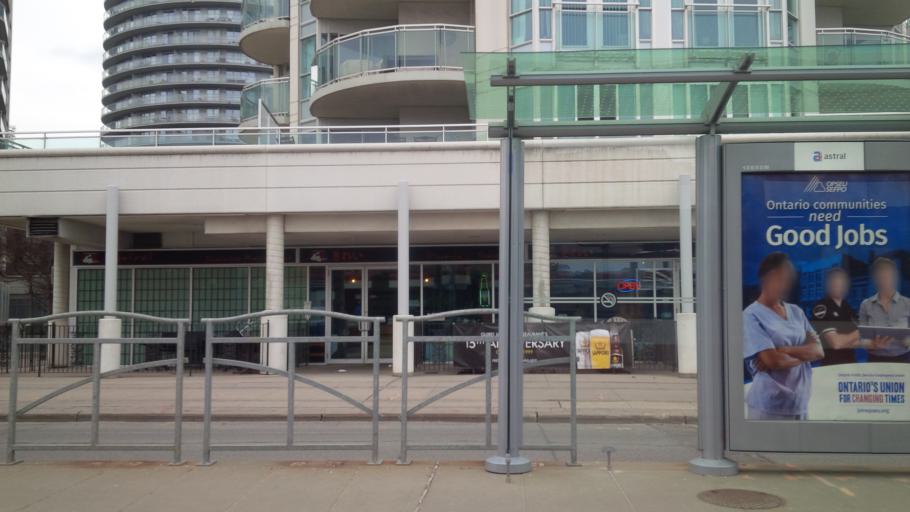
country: CA
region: Ontario
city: Toronto
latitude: 43.6365
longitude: -79.3971
